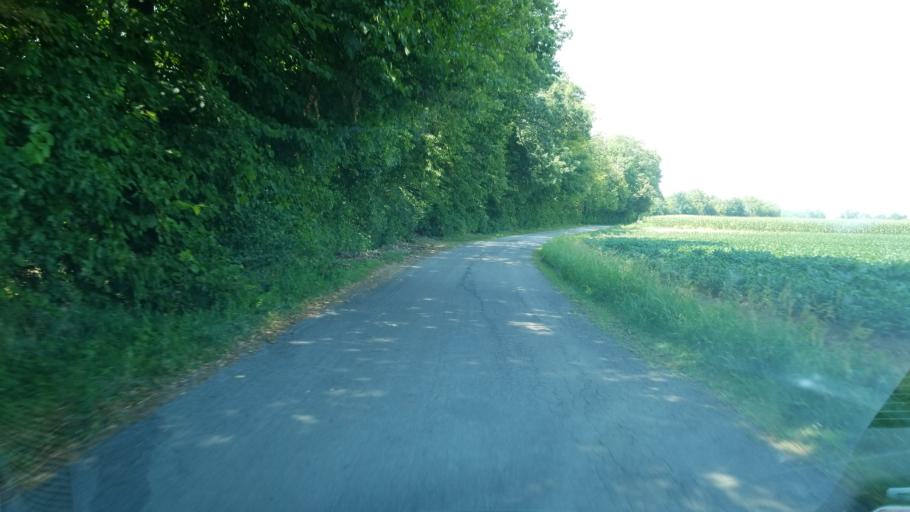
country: US
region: Ohio
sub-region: Marion County
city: Prospect
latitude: 40.3722
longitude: -83.1851
